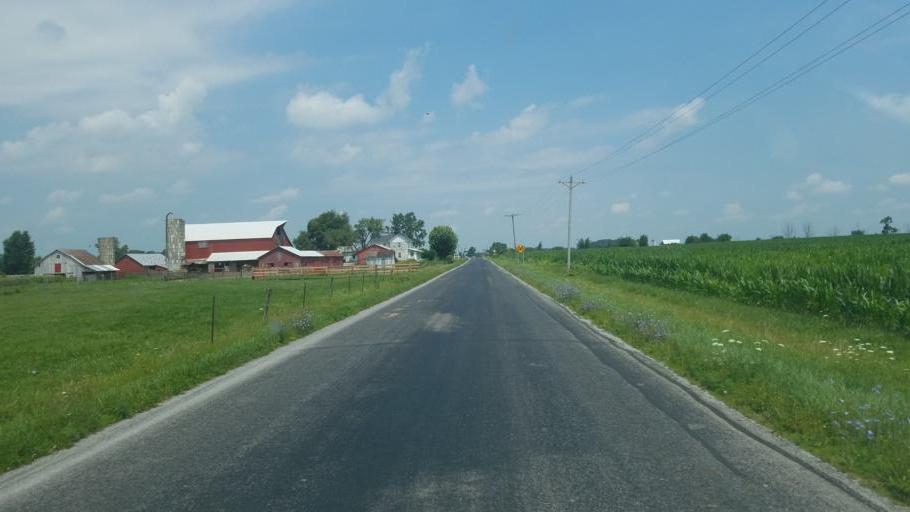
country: US
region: Ohio
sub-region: Hardin County
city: Kenton
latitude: 40.5562
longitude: -83.4408
